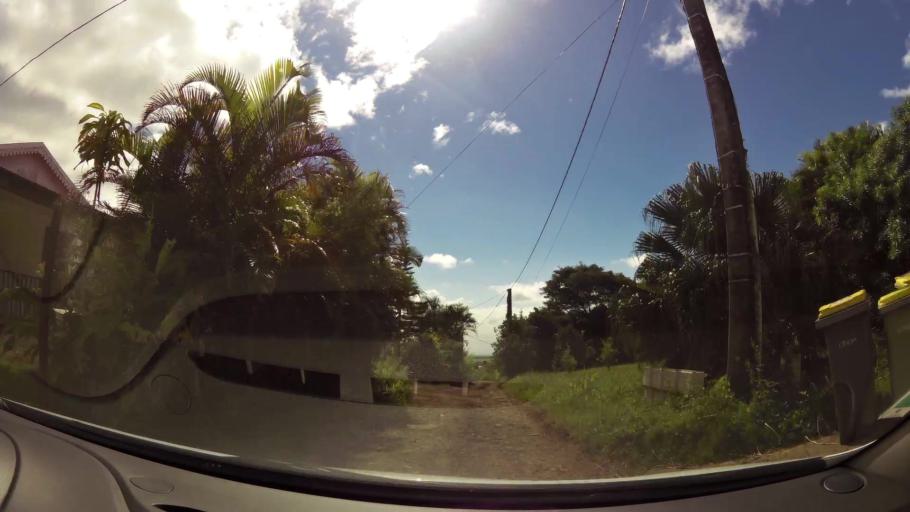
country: RE
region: Reunion
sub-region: Reunion
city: Sainte-Marie
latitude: -20.9282
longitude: 55.5029
